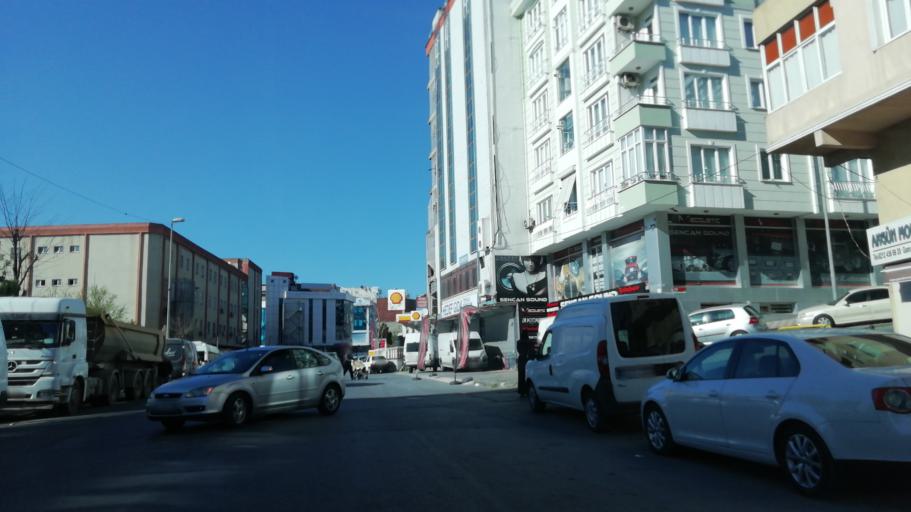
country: TR
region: Istanbul
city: Bagcilar
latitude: 41.0360
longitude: 28.8526
